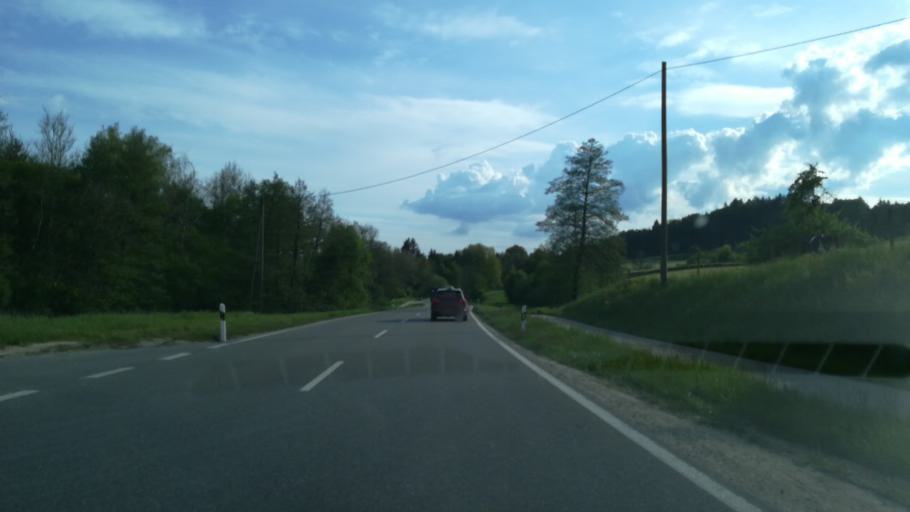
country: DE
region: Baden-Wuerttemberg
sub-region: Freiburg Region
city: Muhlingen
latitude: 47.8898
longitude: 9.0051
